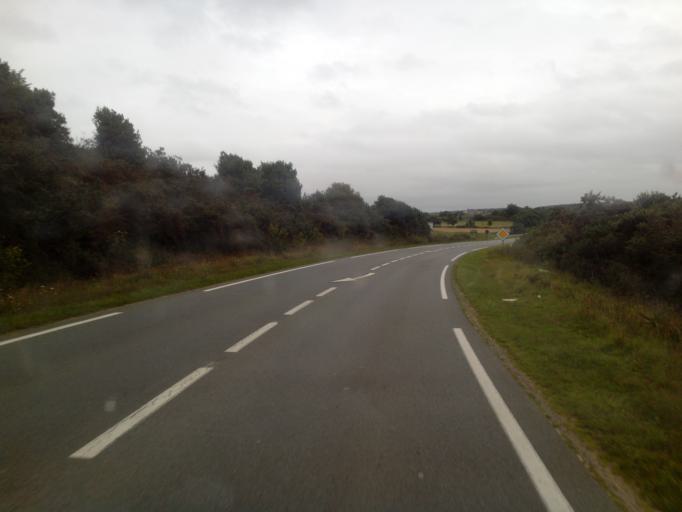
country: FR
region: Brittany
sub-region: Departement des Cotes-d'Armor
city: Lezardrieux
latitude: 48.7785
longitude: -3.1016
